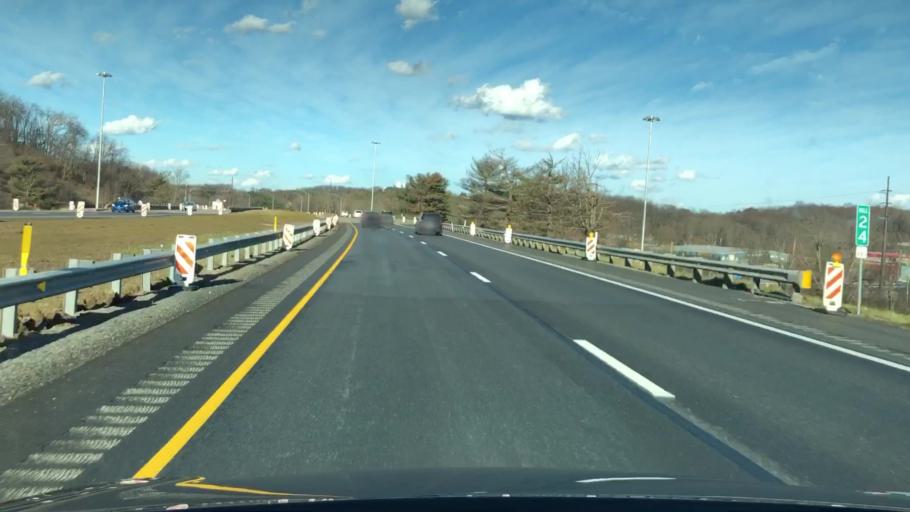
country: US
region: Pennsylvania
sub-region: Armstrong County
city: Freeport
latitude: 40.6665
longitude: -79.7160
